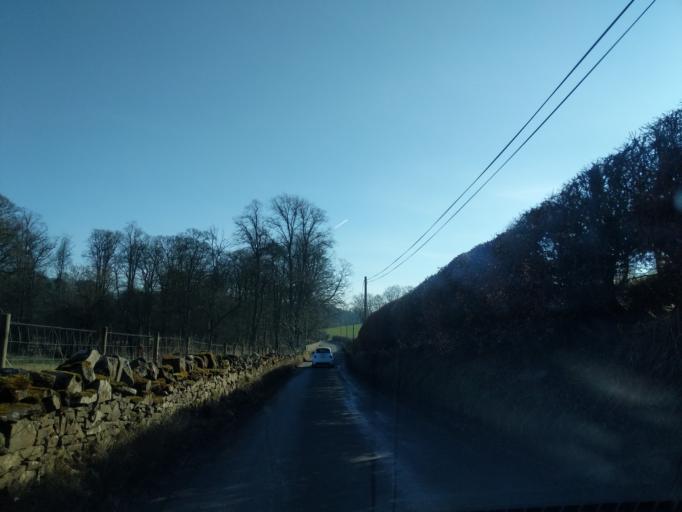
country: GB
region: Scotland
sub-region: South Lanarkshire
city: Lanark
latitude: 55.6816
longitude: -3.8093
